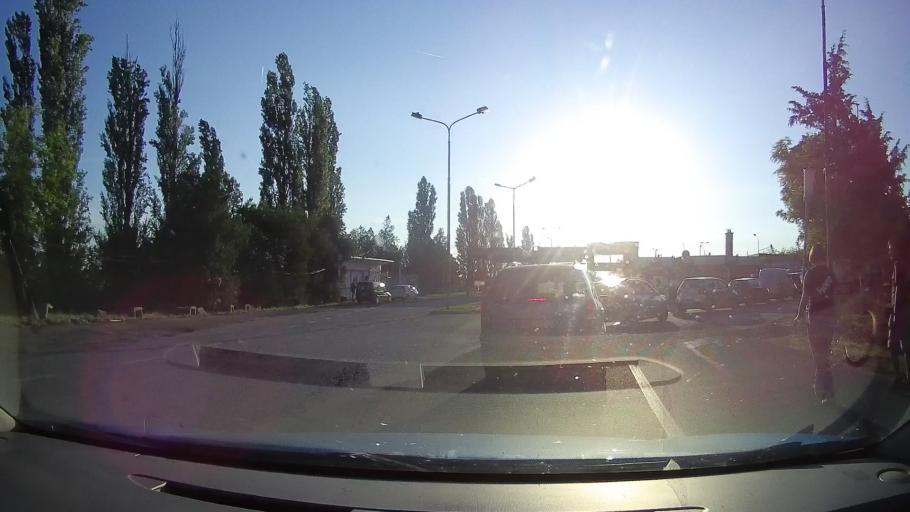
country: RO
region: Timis
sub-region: Comuna Moravita
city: Moravita
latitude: 45.2289
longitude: 21.2775
